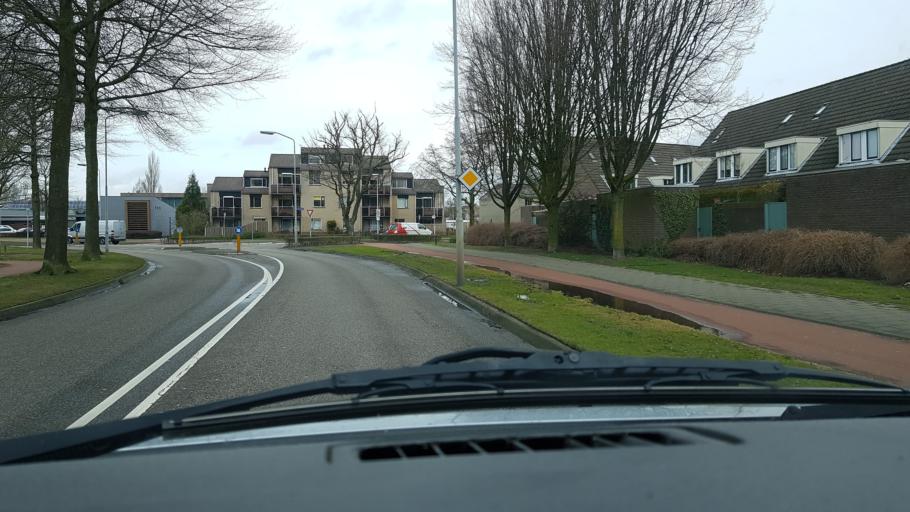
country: NL
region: North Brabant
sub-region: Gemeente Veldhoven
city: Veldhoven
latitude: 51.4260
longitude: 5.3924
